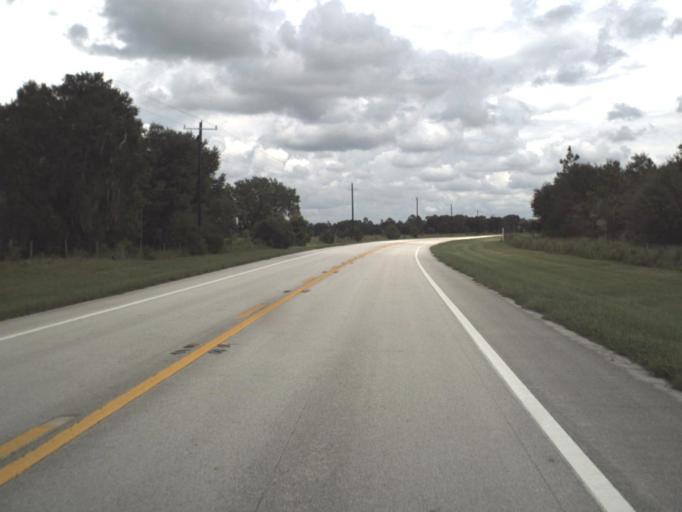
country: US
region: Florida
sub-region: DeSoto County
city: Nocatee
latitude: 27.2065
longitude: -82.0188
